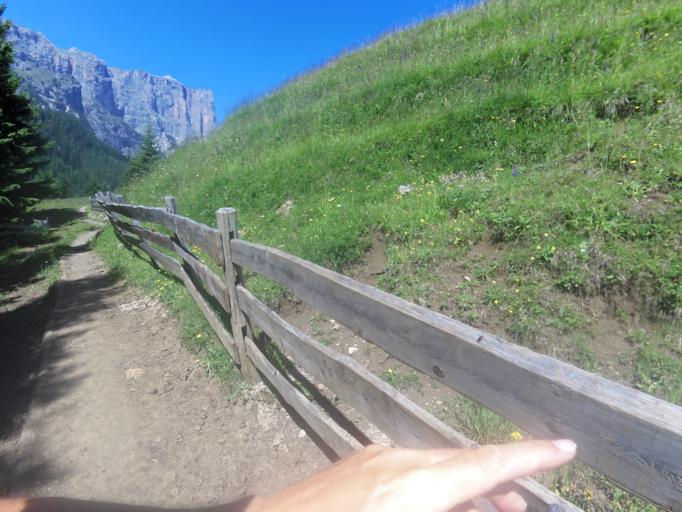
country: IT
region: Trentino-Alto Adige
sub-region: Bolzano
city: Siusi
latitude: 46.5181
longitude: 11.6023
